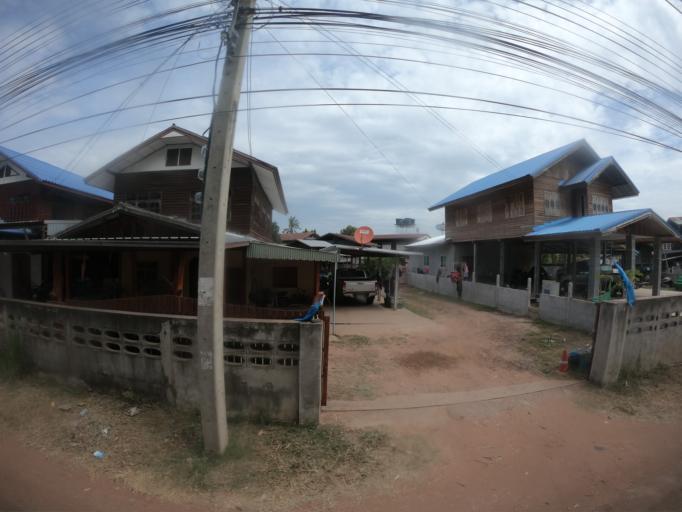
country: TH
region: Maha Sarakham
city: Chiang Yuen
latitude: 16.3492
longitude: 103.1208
